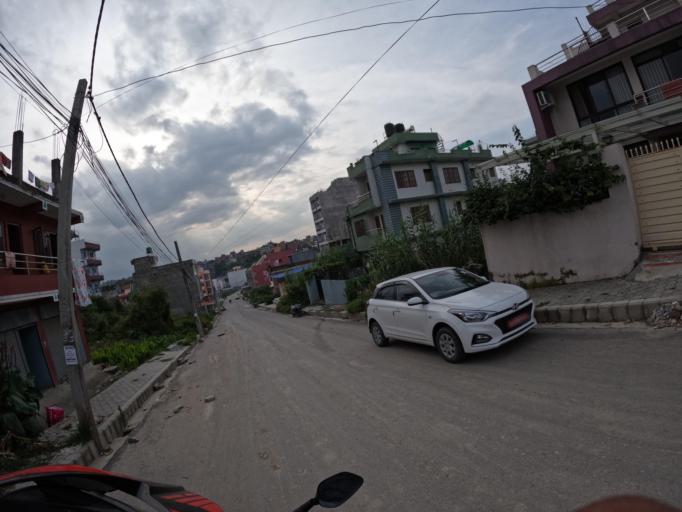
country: NP
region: Central Region
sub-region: Bagmati Zone
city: Bhaktapur
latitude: 27.6790
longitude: 85.3920
